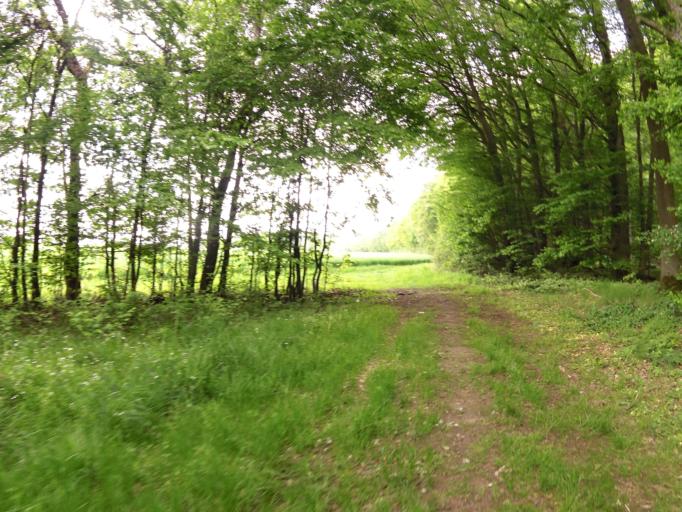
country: DE
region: Bavaria
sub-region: Regierungsbezirk Unterfranken
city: Kist
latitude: 49.7358
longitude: 9.8522
